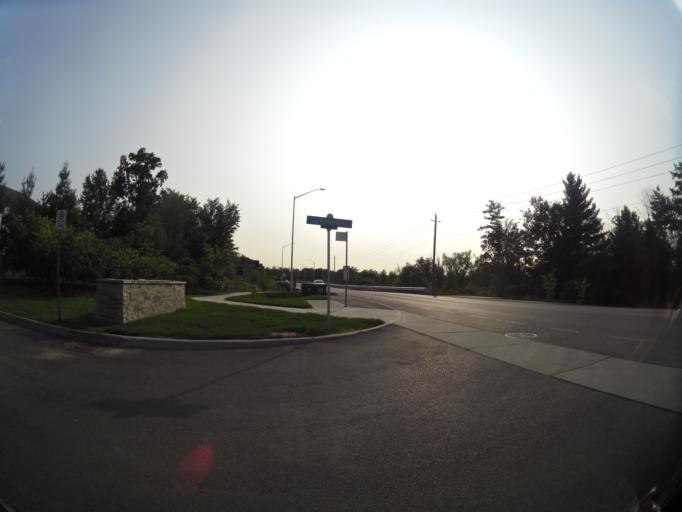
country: CA
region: Quebec
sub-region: Outaouais
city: Gatineau
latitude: 45.4934
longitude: -75.4934
